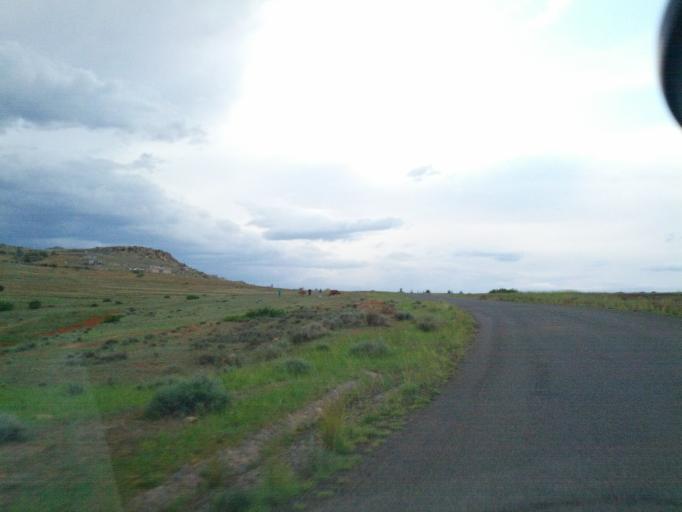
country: LS
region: Qacha's Nek
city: Qacha's Nek
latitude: -30.0511
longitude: 28.3752
